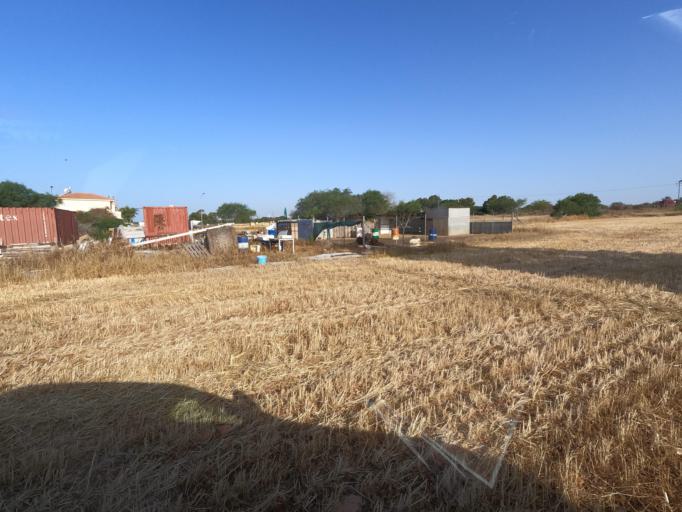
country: CY
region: Ammochostos
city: Liopetri
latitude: 34.9818
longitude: 33.9232
